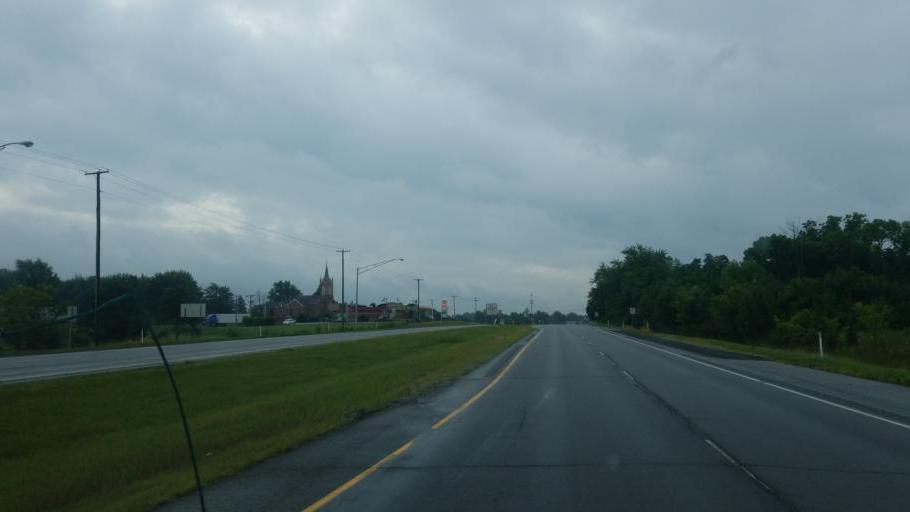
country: US
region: Indiana
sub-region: Allen County
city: New Haven
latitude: 40.9815
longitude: -85.0857
